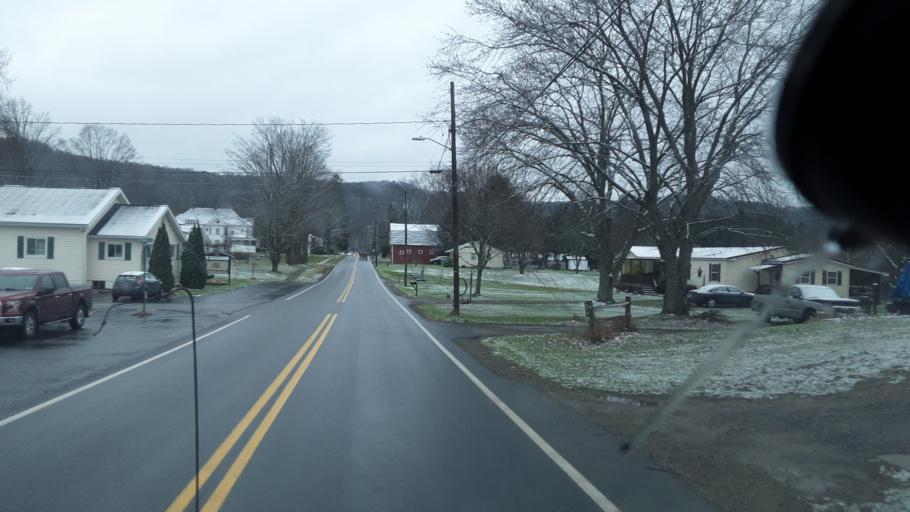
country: US
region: Pennsylvania
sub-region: Potter County
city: Shinglehouse
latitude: 41.9658
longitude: -78.1913
